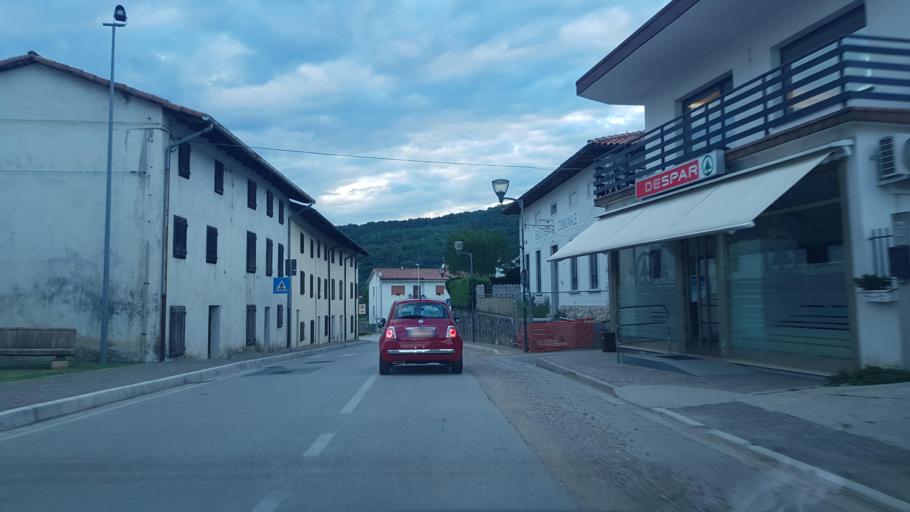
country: IT
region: Friuli Venezia Giulia
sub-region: Provincia di Udine
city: San Giacomo
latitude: 46.1784
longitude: 12.9787
